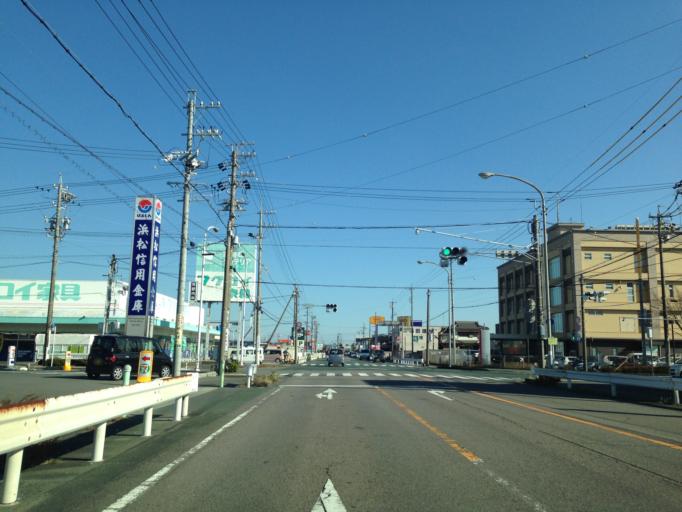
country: JP
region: Shizuoka
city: Fukuroi
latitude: 34.7513
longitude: 137.9247
